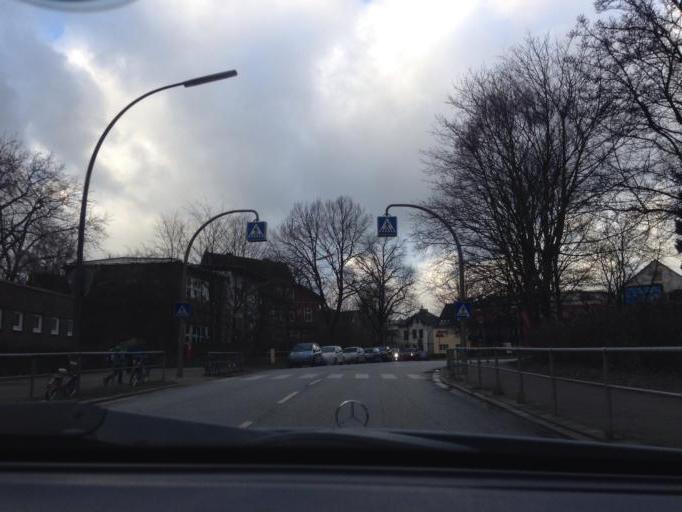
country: DE
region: Hamburg
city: Marienthal
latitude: 53.5719
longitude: 10.0808
